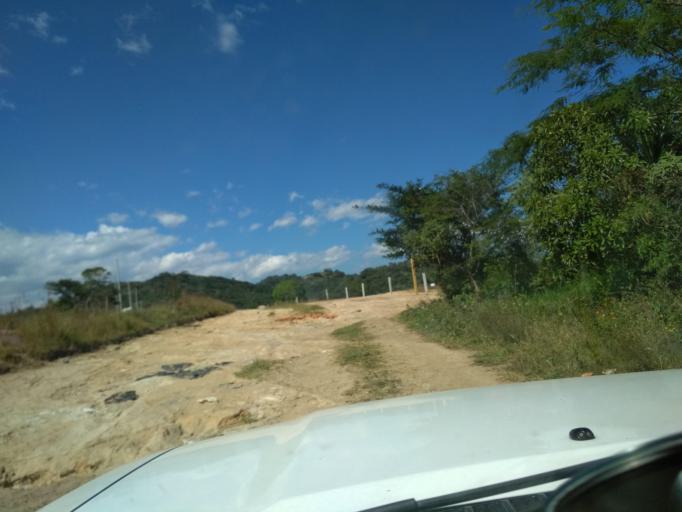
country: MX
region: Veracruz
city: El Castillo
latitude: 19.5475
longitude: -96.8548
